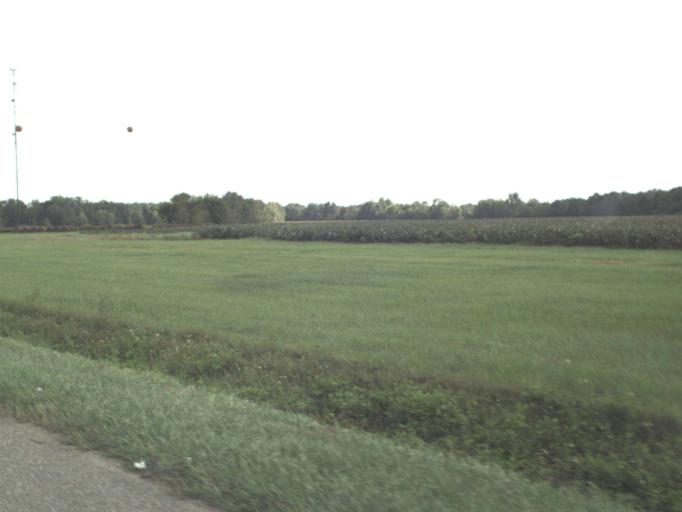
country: US
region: Florida
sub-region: Calhoun County
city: Blountstown
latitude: 30.6017
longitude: -85.1397
